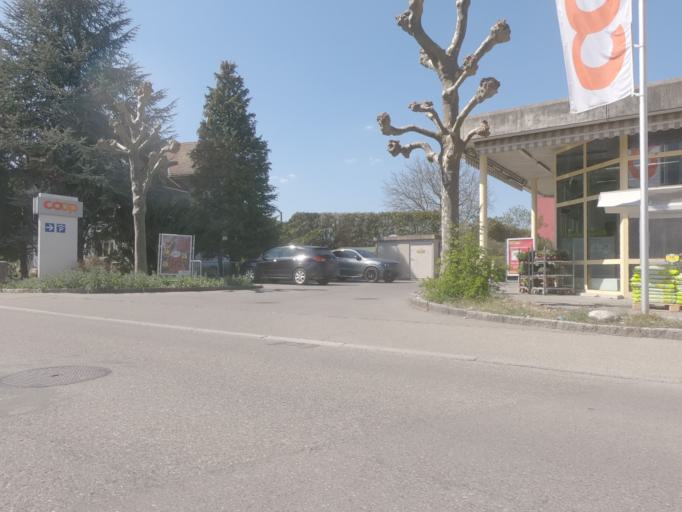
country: CH
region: Bern
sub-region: Seeland District
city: Worben
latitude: 47.0993
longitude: 7.3207
